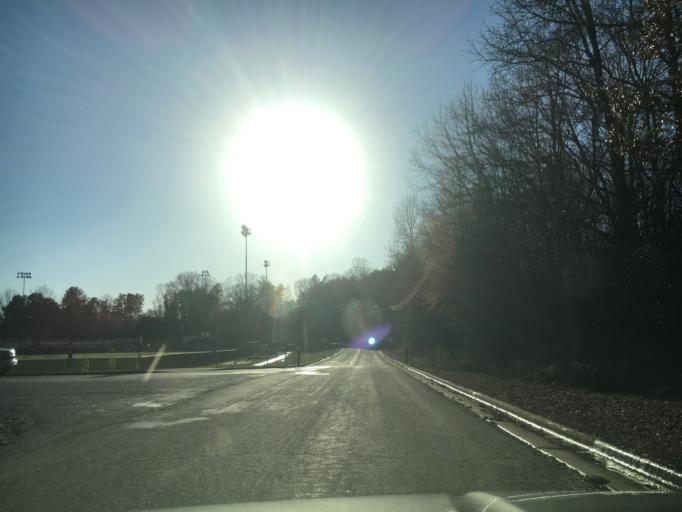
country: US
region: Virginia
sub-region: Halifax County
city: South Boston
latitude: 36.7314
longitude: -78.9118
